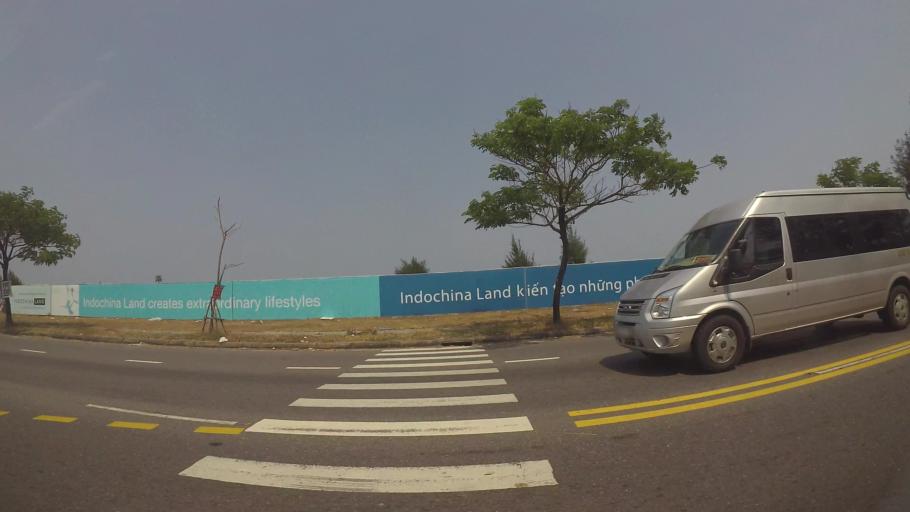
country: VN
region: Da Nang
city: Ngu Hanh Son
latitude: 15.9855
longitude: 108.2735
